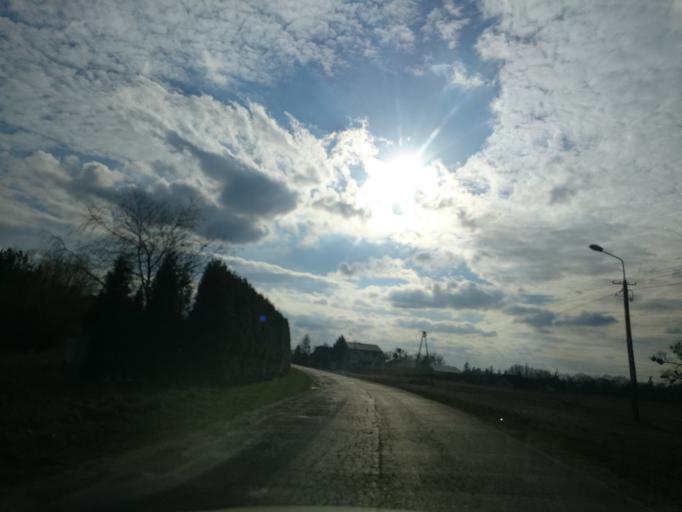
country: PL
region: Kujawsko-Pomorskie
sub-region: Powiat torunski
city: Lubicz Gorny
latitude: 53.0377
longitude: 18.7900
